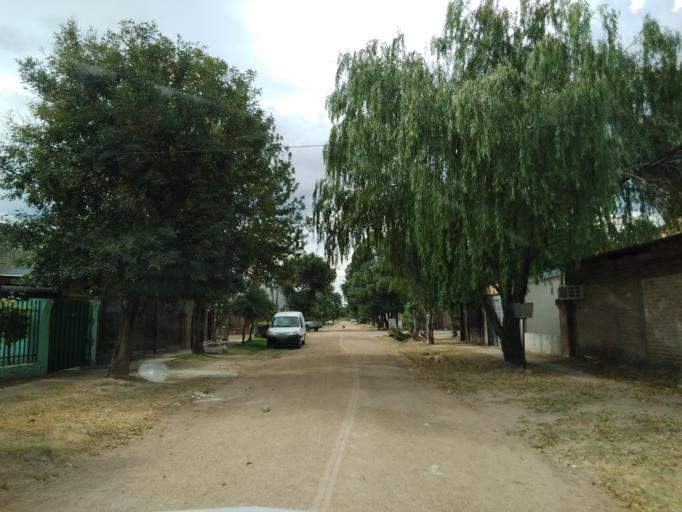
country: AR
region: Corrientes
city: Corrientes
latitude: -27.5205
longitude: -58.7925
